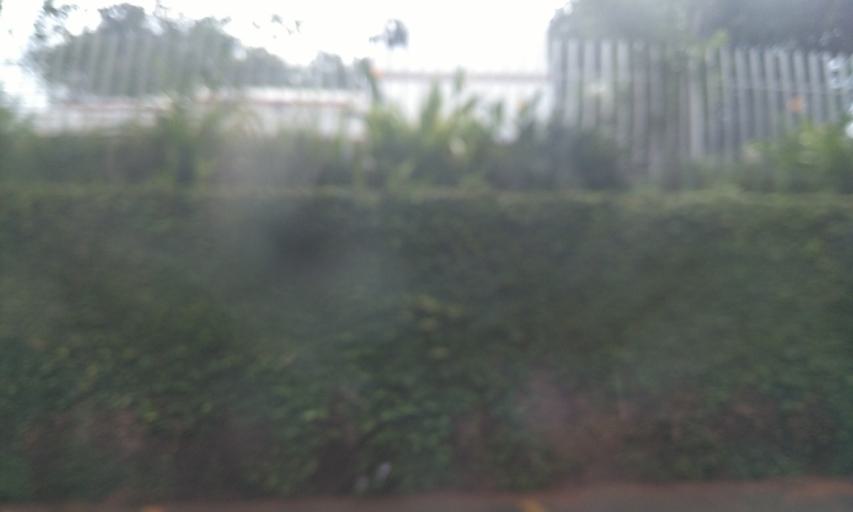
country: UG
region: Central Region
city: Kampala Central Division
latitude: 0.3318
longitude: 32.5862
